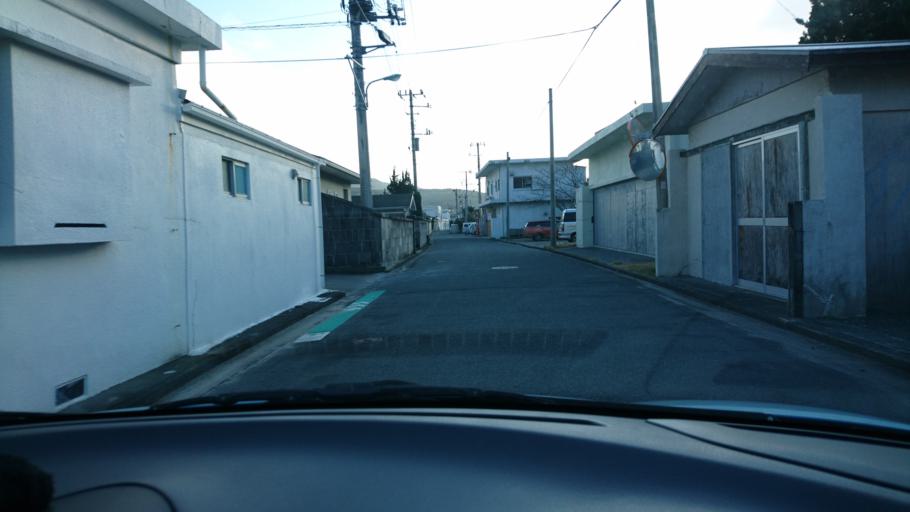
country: JP
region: Shizuoka
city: Shimoda
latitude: 34.3814
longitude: 139.2556
